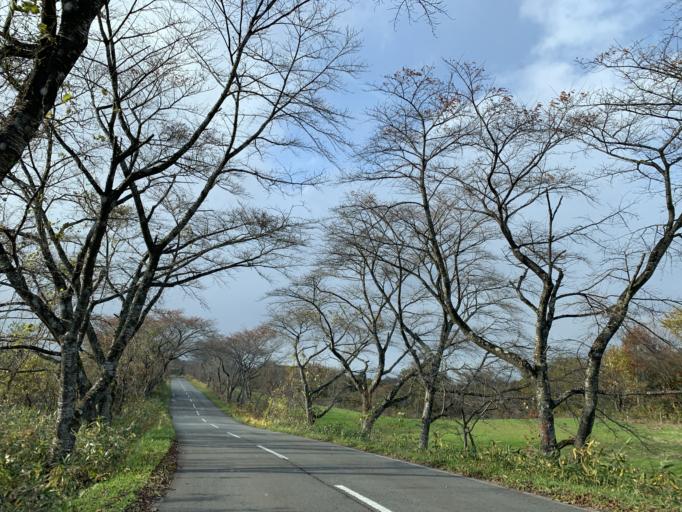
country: JP
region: Iwate
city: Mizusawa
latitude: 39.0404
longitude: 141.0794
